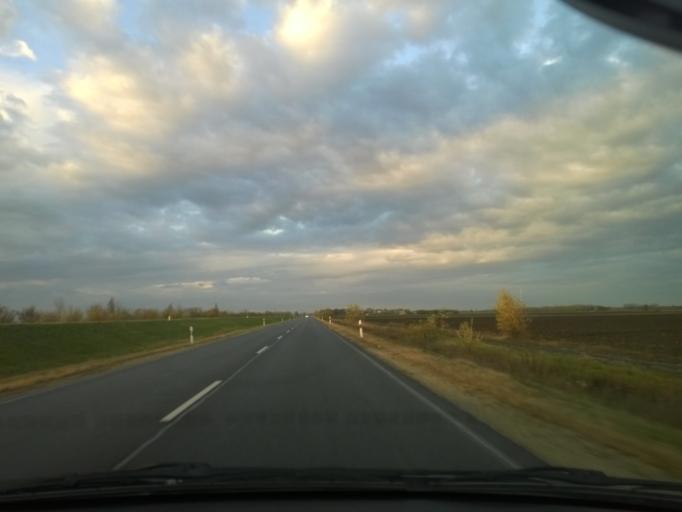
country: HU
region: Bacs-Kiskun
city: Solt
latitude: 46.7686
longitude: 19.0080
